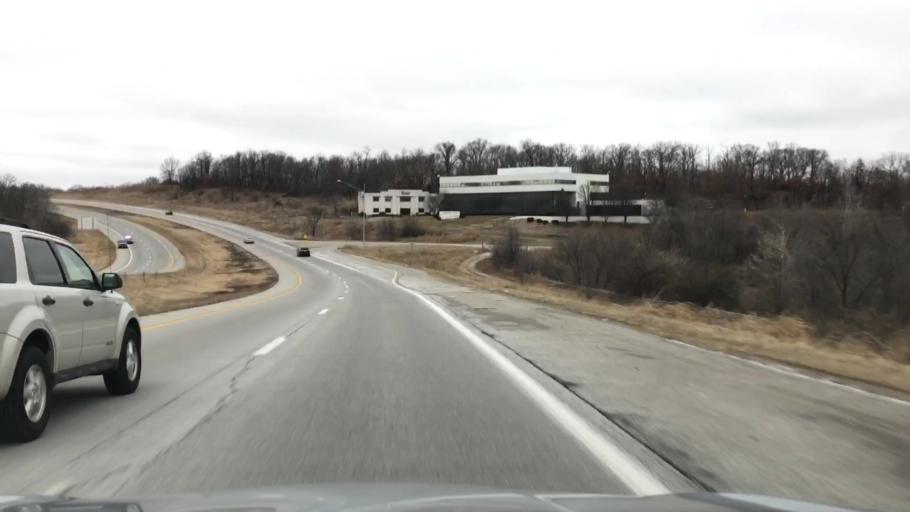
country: US
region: Missouri
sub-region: Jackson County
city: East Independence
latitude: 39.0553
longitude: -94.3666
